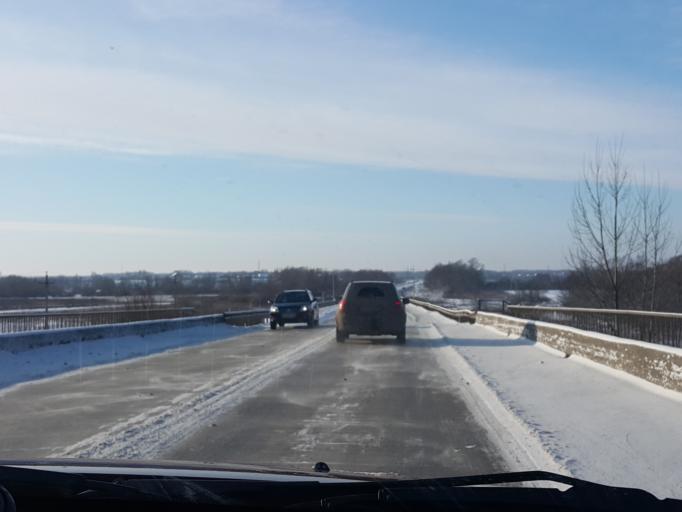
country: RU
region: Tambov
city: Znamenka
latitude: 52.4155
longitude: 41.4838
